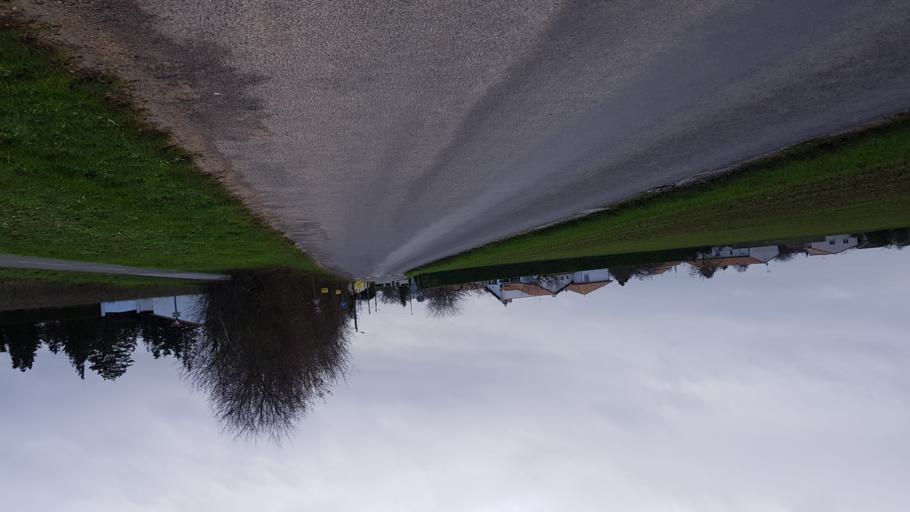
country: FR
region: Poitou-Charentes
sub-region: Departement de la Vienne
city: Avanton
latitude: 46.6677
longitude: 0.3135
